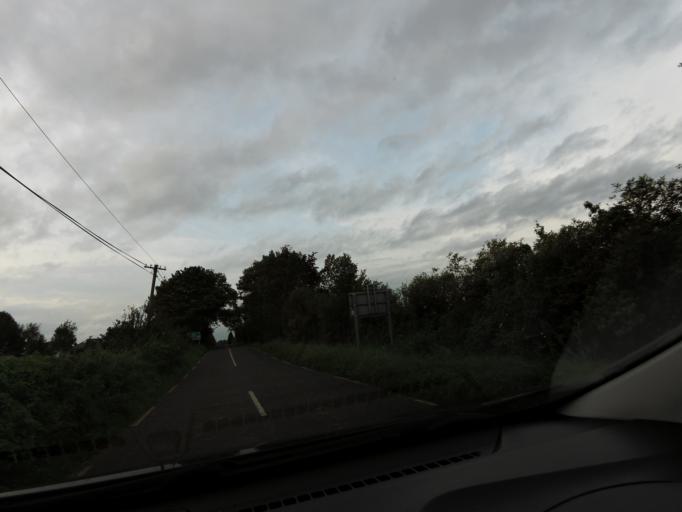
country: IE
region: Leinster
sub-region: Uibh Fhaili
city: Ferbane
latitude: 53.2604
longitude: -7.8352
